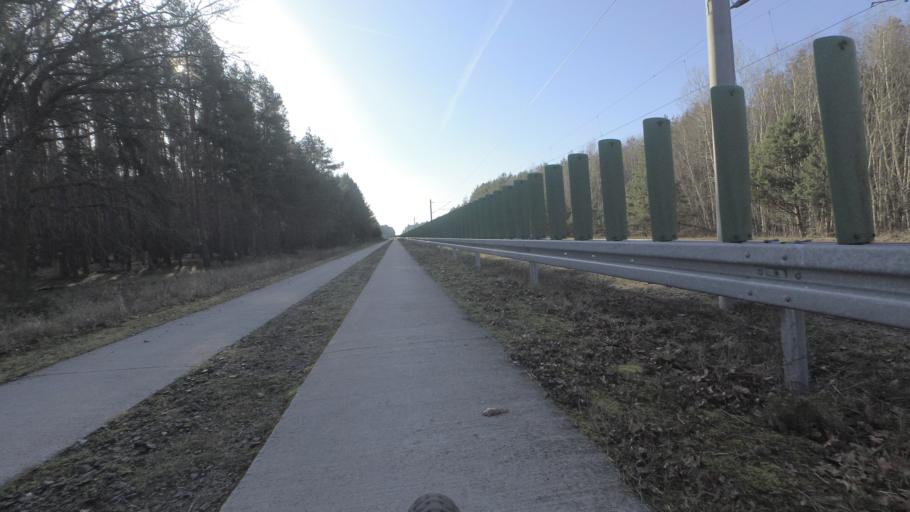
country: DE
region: Brandenburg
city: Trebbin
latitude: 52.1668
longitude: 13.2213
